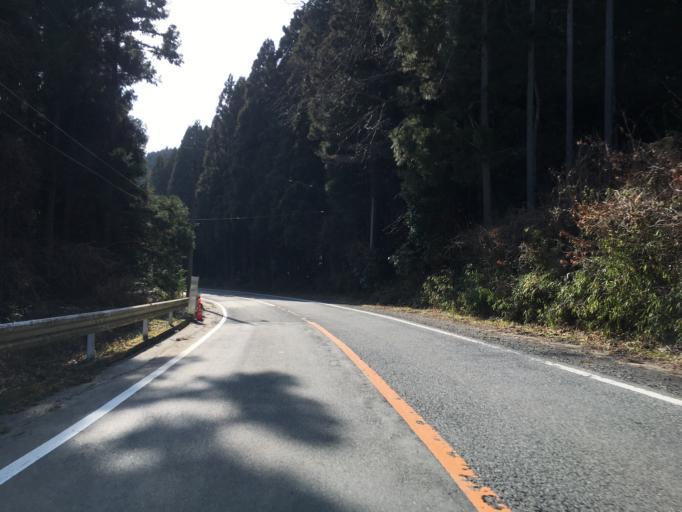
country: JP
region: Ibaraki
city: Daigo
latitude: 36.7347
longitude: 140.5153
